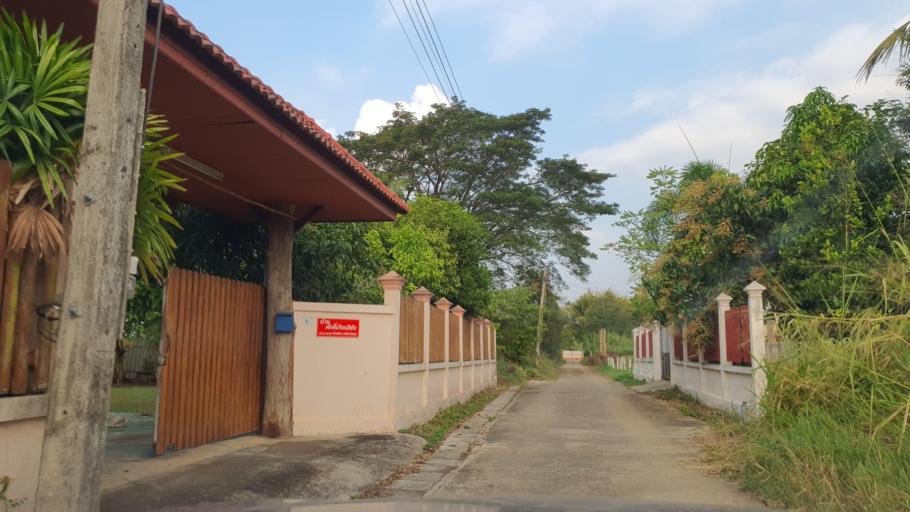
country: TH
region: Chiang Mai
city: San Kamphaeng
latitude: 18.7421
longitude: 99.1019
